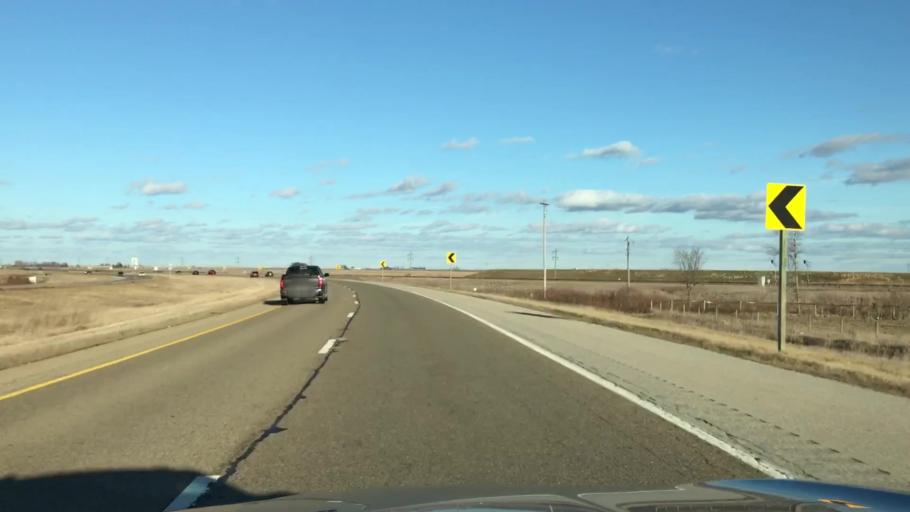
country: US
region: Illinois
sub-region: McLean County
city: Lexington
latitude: 40.6607
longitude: -88.7756
